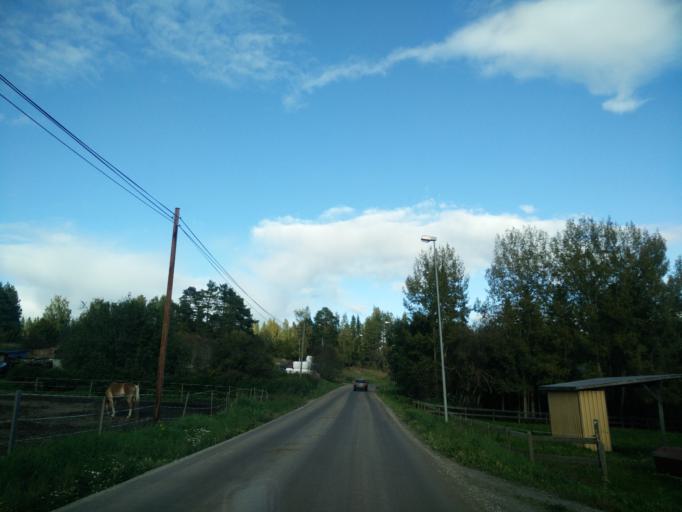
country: SE
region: Vaesternorrland
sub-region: Sundsvalls Kommun
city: Matfors
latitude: 62.3354
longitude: 16.9950
